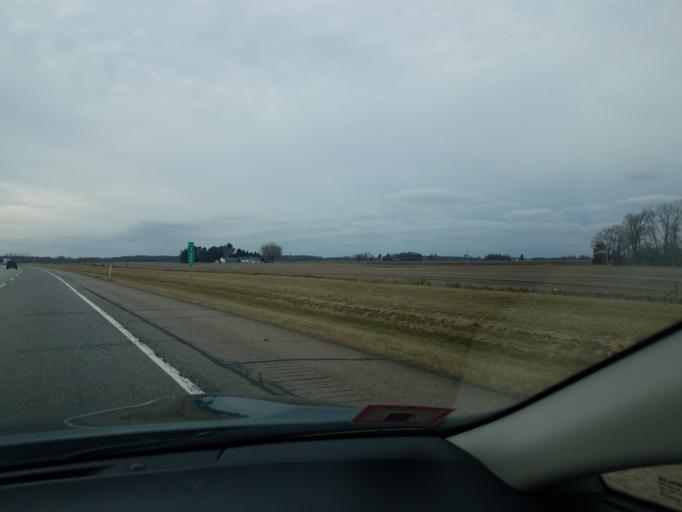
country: US
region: Michigan
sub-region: Saint Joseph County
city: Sturgis
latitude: 41.7490
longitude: -85.3436
